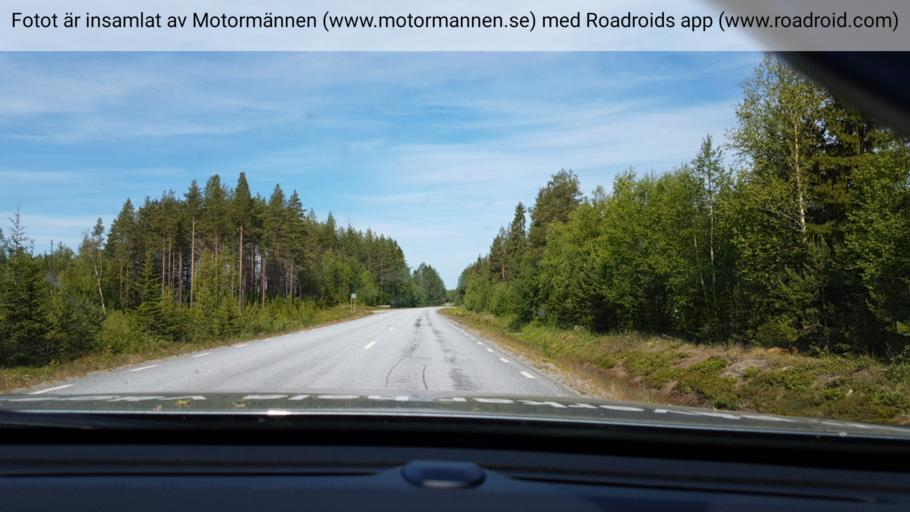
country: SE
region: Vaesterbotten
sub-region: Asele Kommun
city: Asele
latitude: 64.1859
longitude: 17.1831
